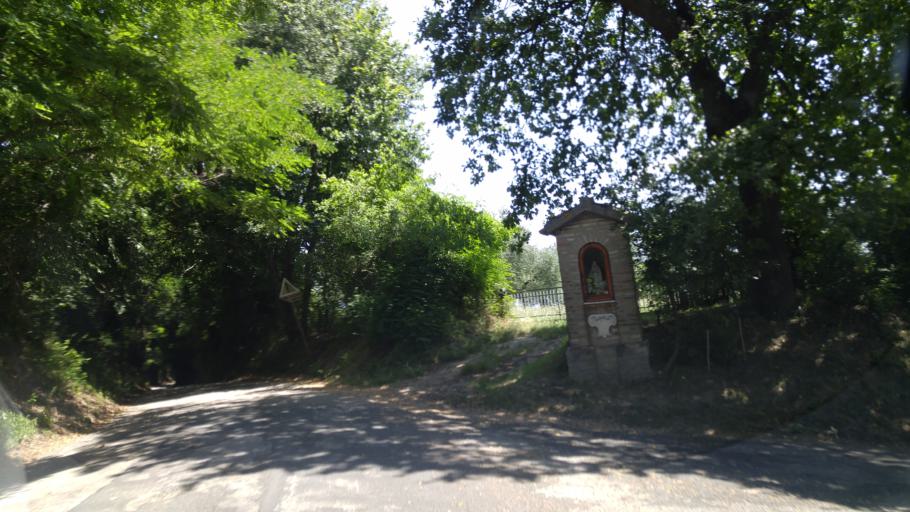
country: IT
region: The Marches
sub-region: Provincia di Pesaro e Urbino
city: Centinarola
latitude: 43.8227
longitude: 12.9805
